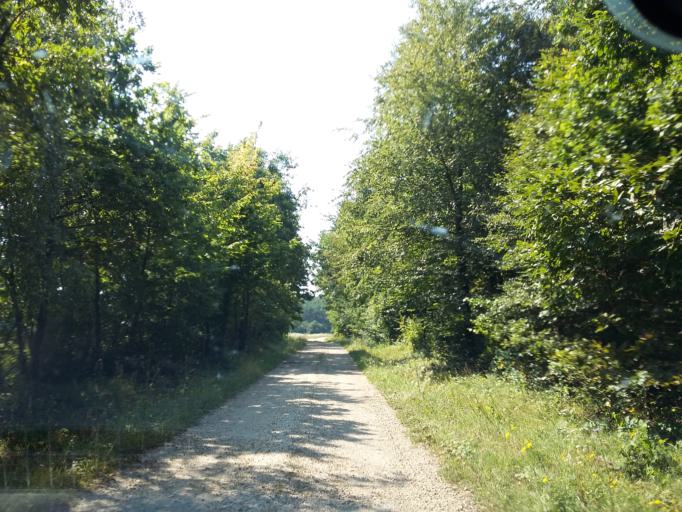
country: SI
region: Hodos-Hodos
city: Hodos
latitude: 46.8438
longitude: 16.3202
